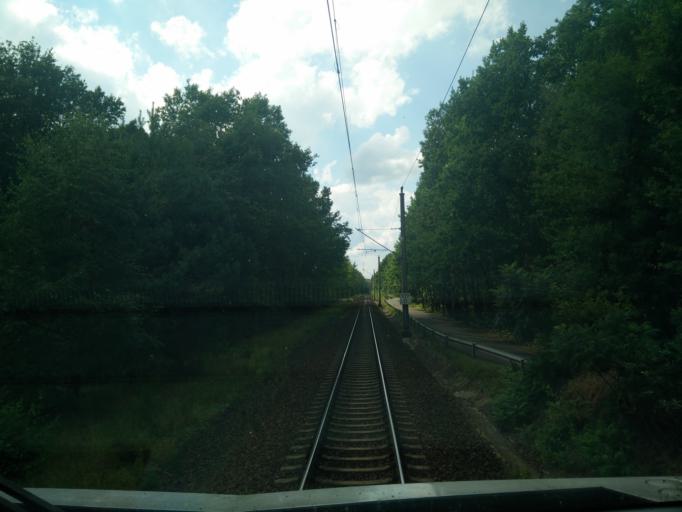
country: DE
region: Brandenburg
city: Kolkwitz
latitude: 51.7587
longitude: 14.2433
